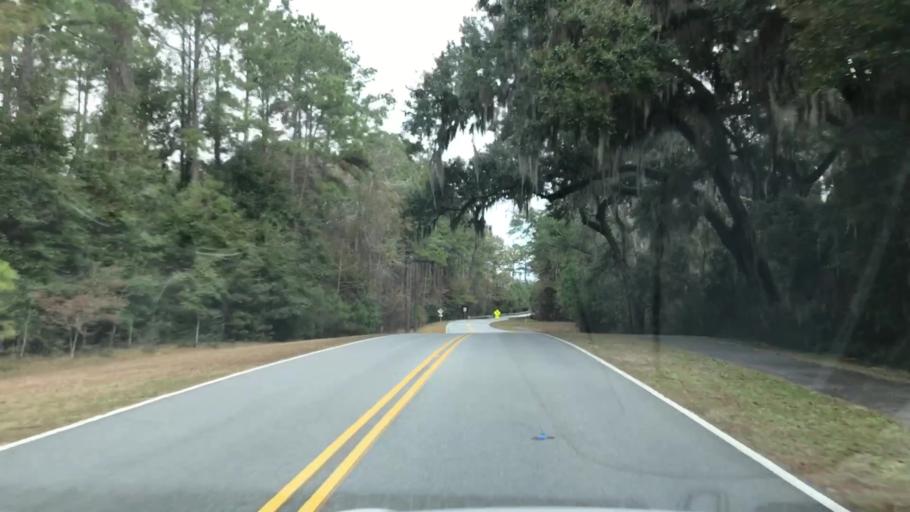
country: US
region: South Carolina
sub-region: Beaufort County
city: Bluffton
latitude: 32.2785
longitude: -80.9274
